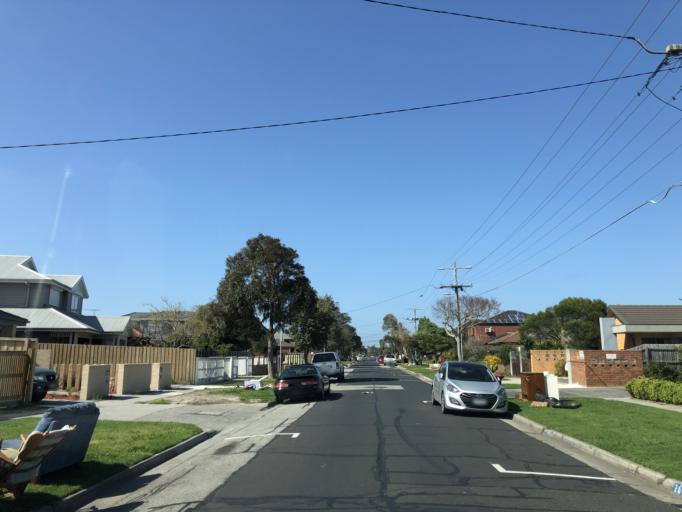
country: AU
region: Victoria
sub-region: Kingston
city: Bonbeach
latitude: -38.0737
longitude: 145.1244
